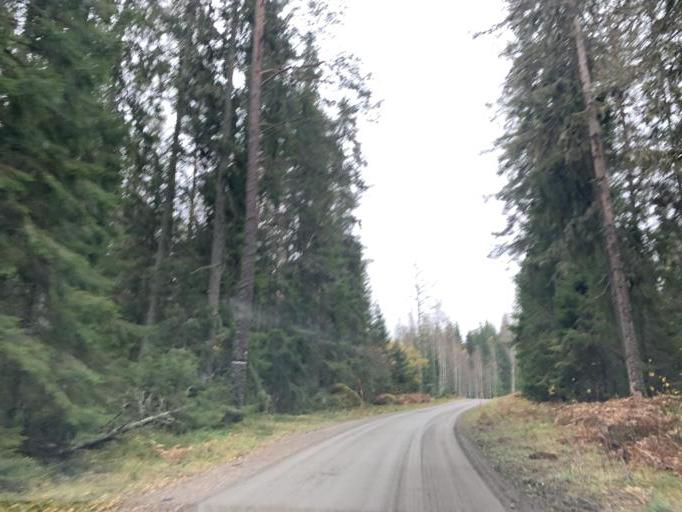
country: SE
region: Vaestmanland
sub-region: Surahammars Kommun
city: Ramnas
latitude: 59.7211
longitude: 16.0946
